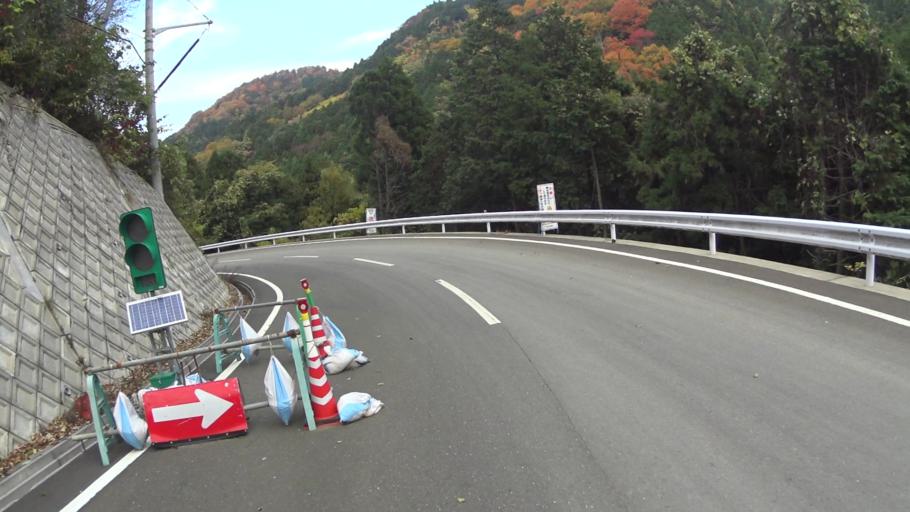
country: JP
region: Kyoto
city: Maizuru
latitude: 35.5572
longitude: 135.4404
